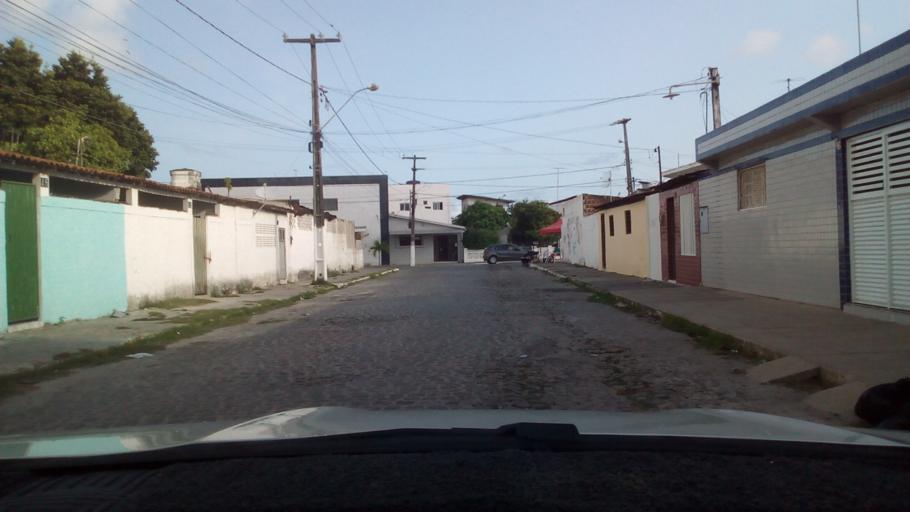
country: BR
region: Paraiba
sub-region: Cabedelo
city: Cabedelo
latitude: -6.9690
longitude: -34.8349
